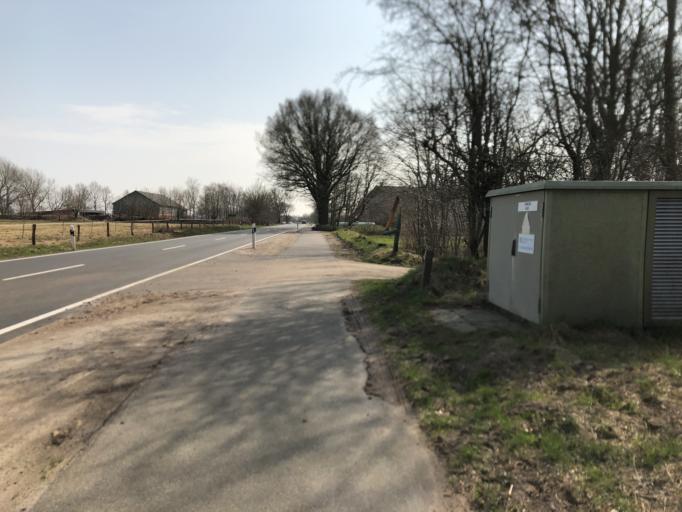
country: DE
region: Schleswig-Holstein
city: Wanderup
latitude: 54.6856
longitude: 9.3600
